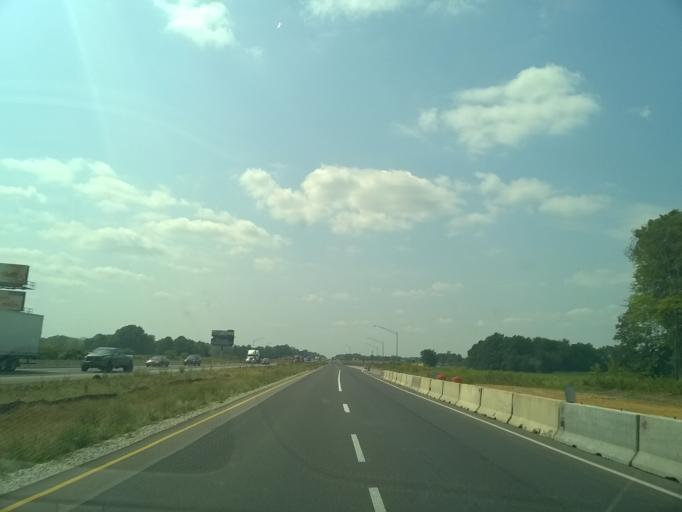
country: US
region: Indiana
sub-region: Vigo County
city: Seelyville
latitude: 39.4308
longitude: -87.3259
